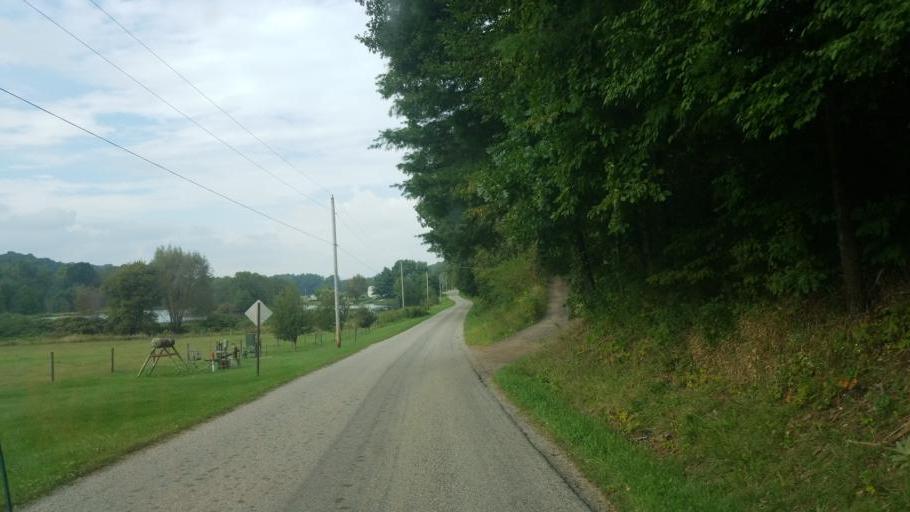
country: US
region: Ohio
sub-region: Wayne County
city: Wooster
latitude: 40.9048
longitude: -82.0069
